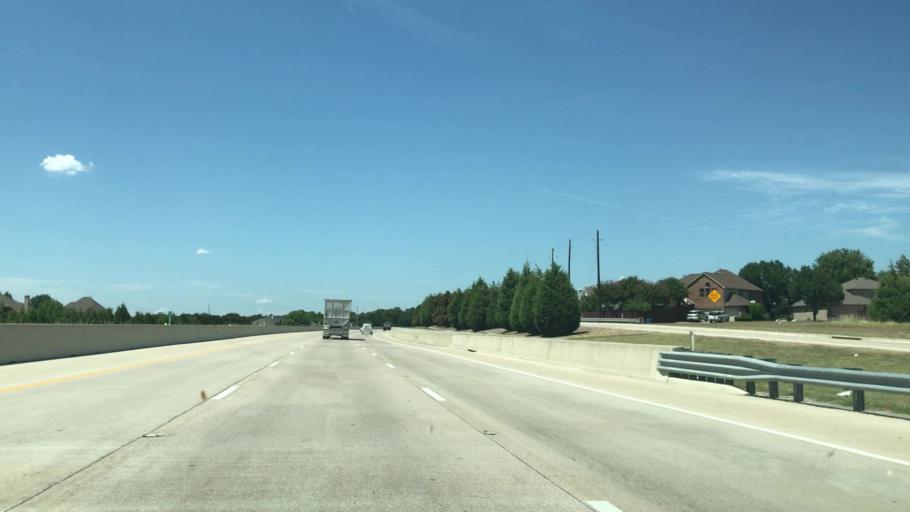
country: US
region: Texas
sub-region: Dallas County
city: Rowlett
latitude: 32.8806
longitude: -96.5545
